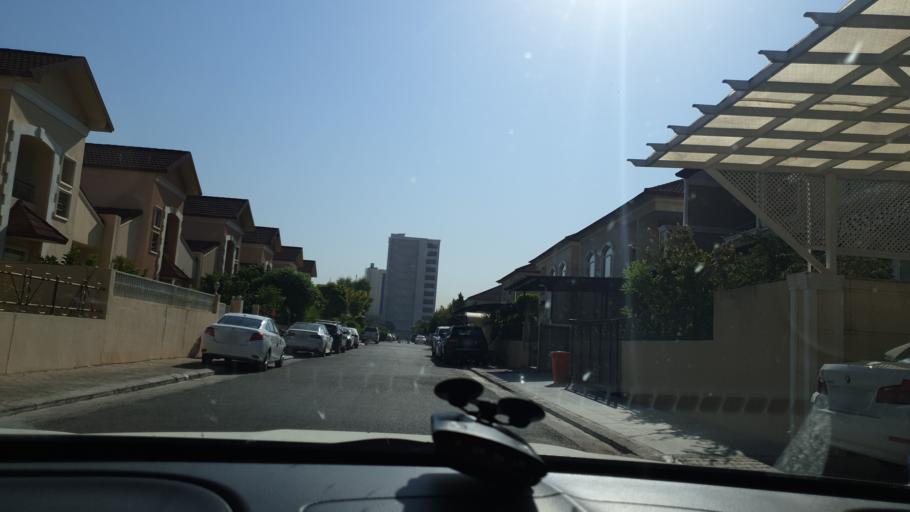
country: IQ
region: Arbil
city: Erbil
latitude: 36.1861
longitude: 43.9670
